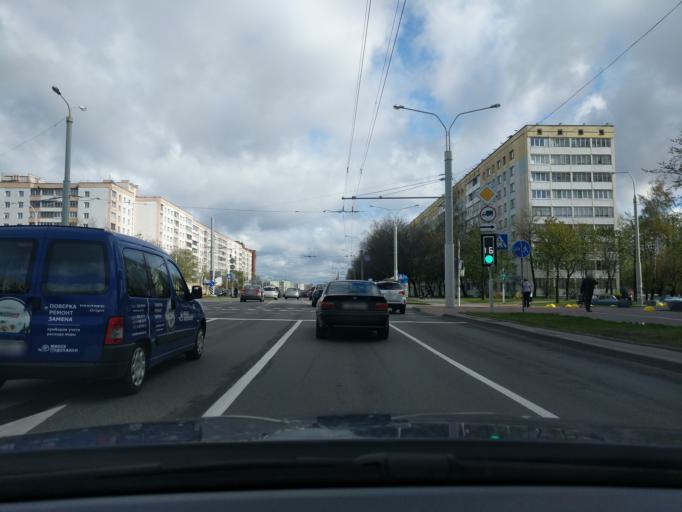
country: BY
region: Minsk
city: Novoye Medvezhino
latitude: 53.9026
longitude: 27.4967
